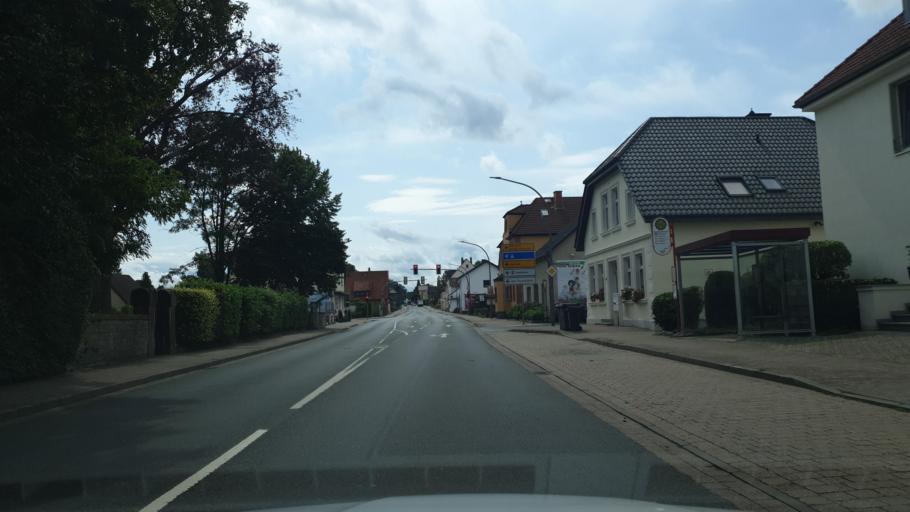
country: DE
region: Lower Saxony
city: Melle
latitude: 52.1985
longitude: 8.3345
